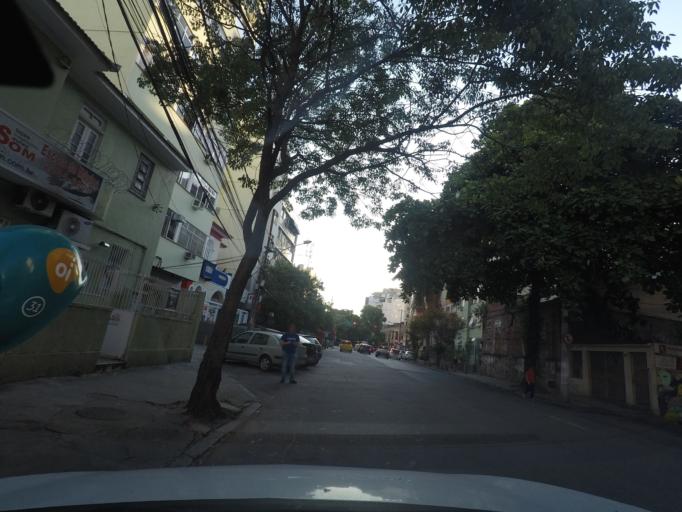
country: BR
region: Rio de Janeiro
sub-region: Rio De Janeiro
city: Rio de Janeiro
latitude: -22.9176
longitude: -43.2236
